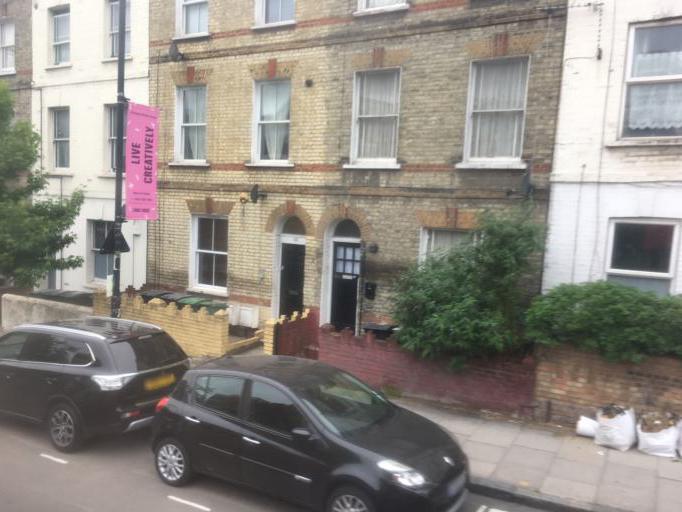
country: GB
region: England
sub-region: Greater London
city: Holloway
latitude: 51.5457
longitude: -0.1265
